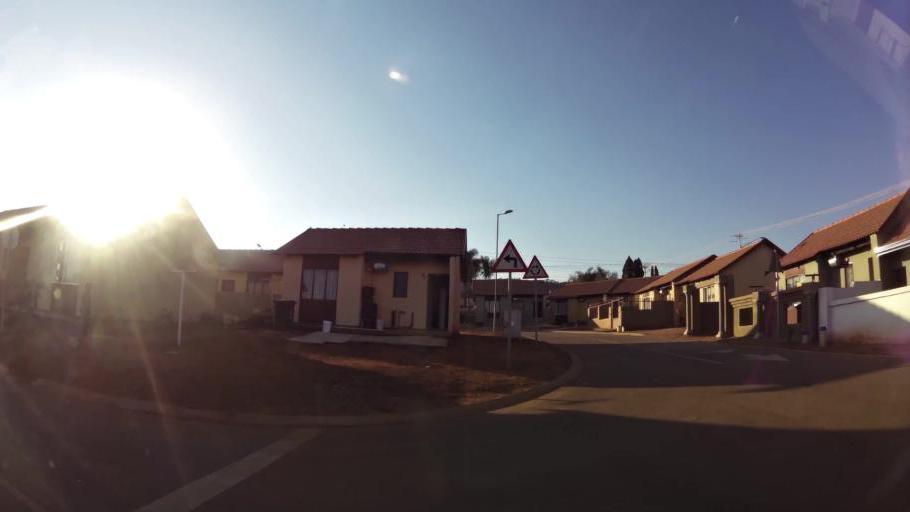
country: ZA
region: Gauteng
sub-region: City of Tshwane Metropolitan Municipality
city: Pretoria
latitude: -25.7371
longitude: 28.1214
